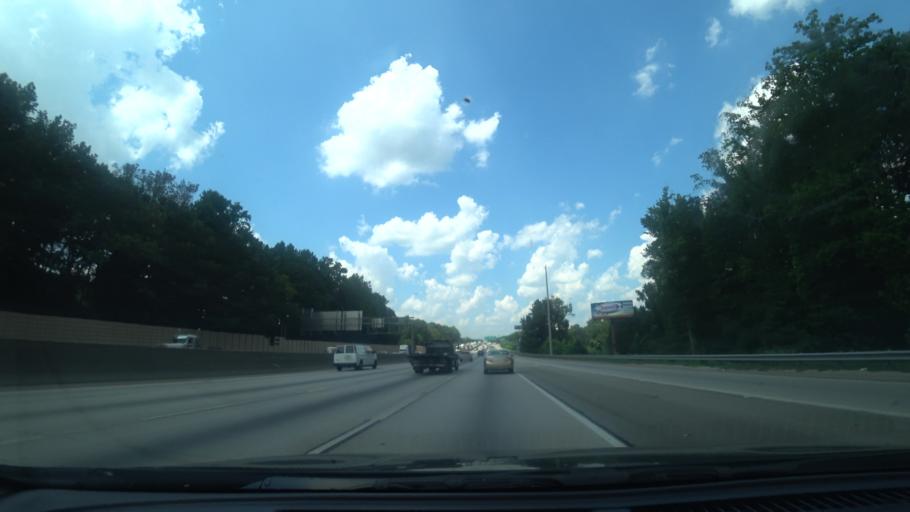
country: US
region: Georgia
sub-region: DeKalb County
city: Clarkston
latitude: 33.8059
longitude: -84.2502
